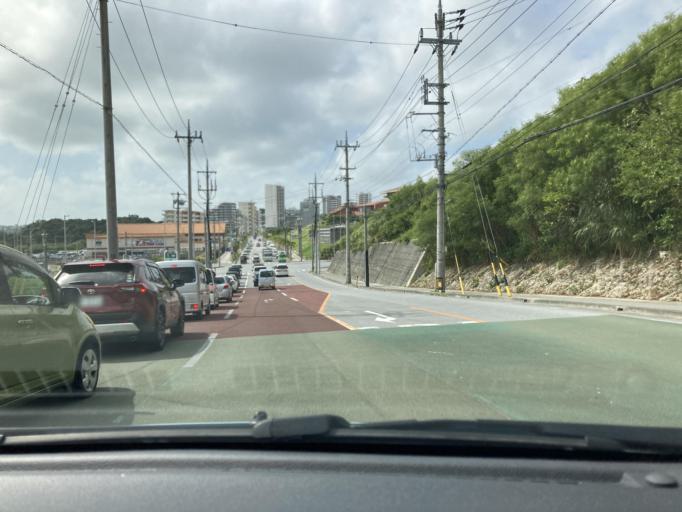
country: JP
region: Okinawa
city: Okinawa
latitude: 26.3173
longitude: 127.7993
